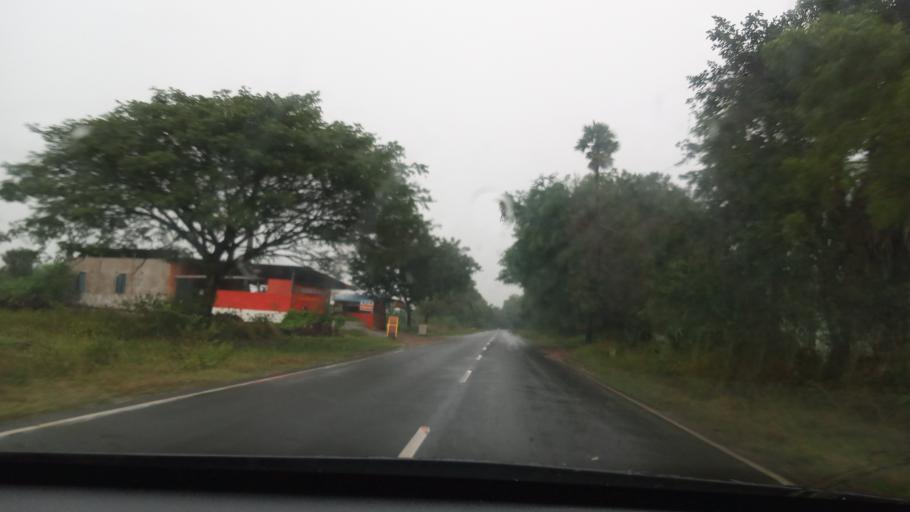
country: IN
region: Tamil Nadu
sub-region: Vellore
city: Kalavai
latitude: 12.8239
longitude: 79.4084
